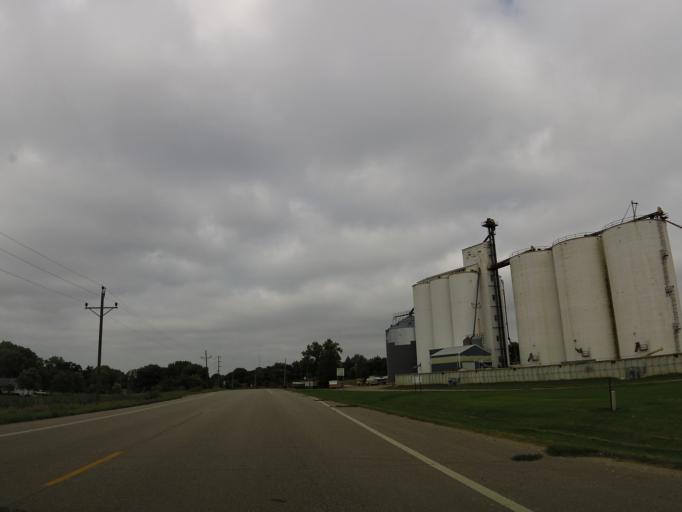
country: US
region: Minnesota
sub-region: Chippewa County
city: Montevideo
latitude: 44.9161
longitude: -95.6948
